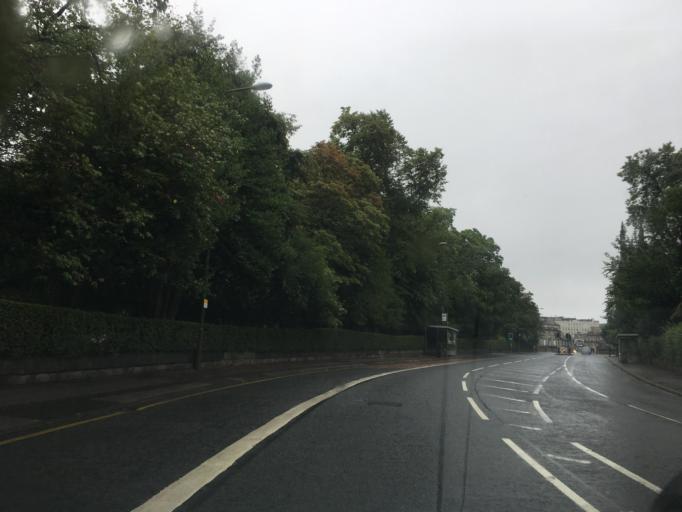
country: GB
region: Scotland
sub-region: Edinburgh
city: Edinburgh
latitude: 55.9549
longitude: -3.2158
